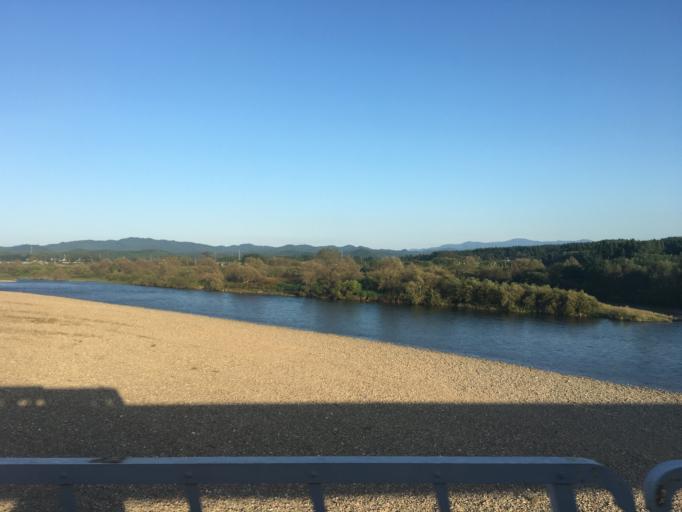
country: JP
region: Akita
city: Takanosu
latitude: 40.2116
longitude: 140.3536
